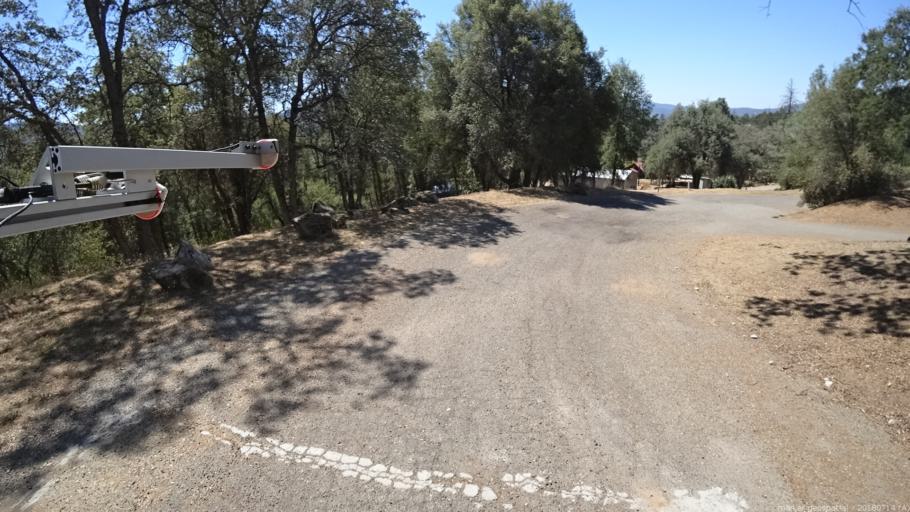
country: US
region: California
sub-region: Madera County
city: Oakhurst
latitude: 37.3730
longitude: -119.6305
